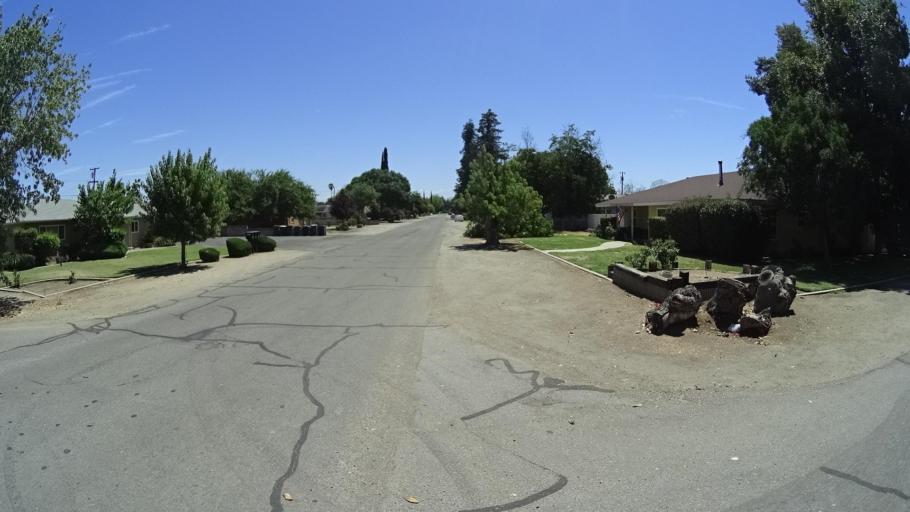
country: US
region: California
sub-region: Fresno County
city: Sunnyside
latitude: 36.7478
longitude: -119.7296
